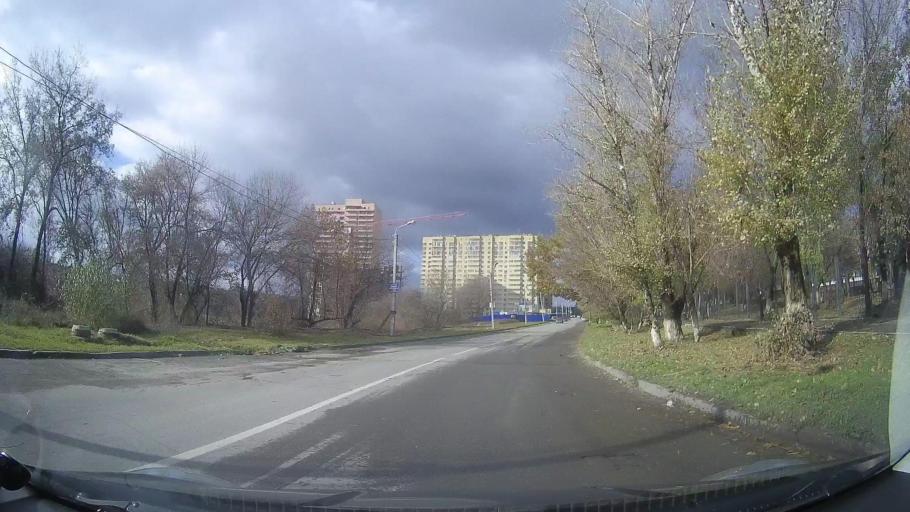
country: RU
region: Rostov
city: Severnyy
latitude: 47.2894
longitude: 39.6903
